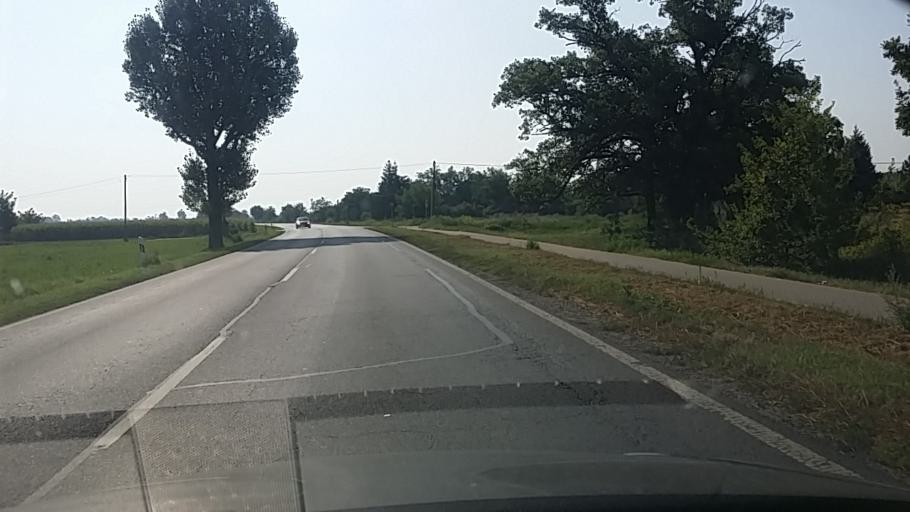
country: HU
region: Bekes
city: Kondoros
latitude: 46.7343
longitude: 20.8956
